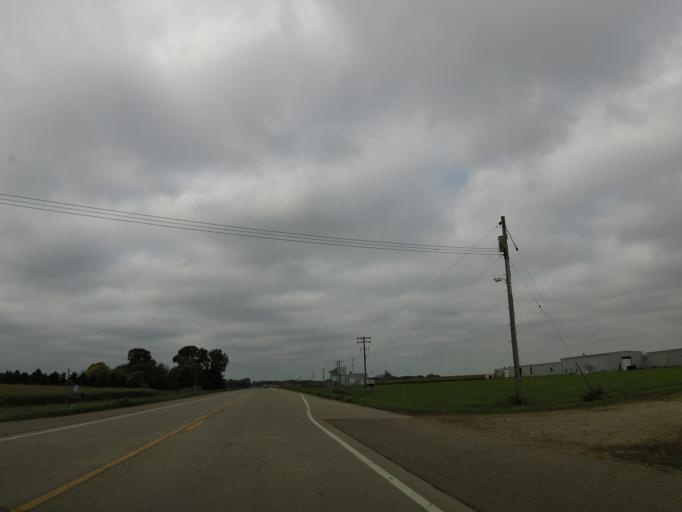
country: US
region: Minnesota
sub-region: Renville County
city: Renville
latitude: 44.7892
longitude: -95.1860
